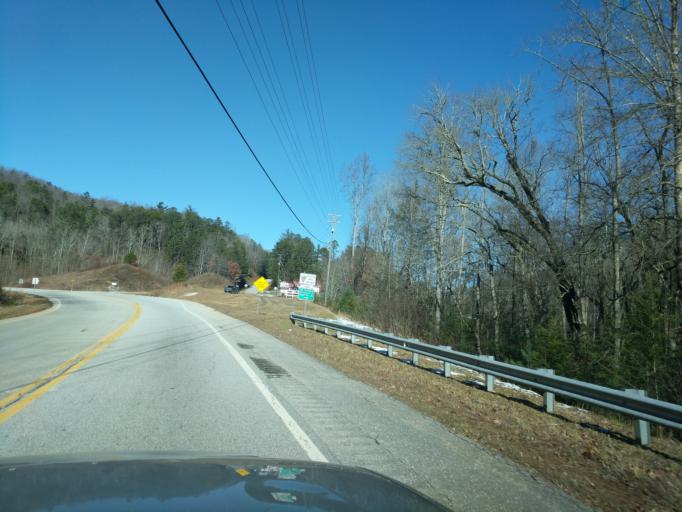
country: US
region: Georgia
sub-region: Rabun County
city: Clayton
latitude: 34.8636
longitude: -83.5185
